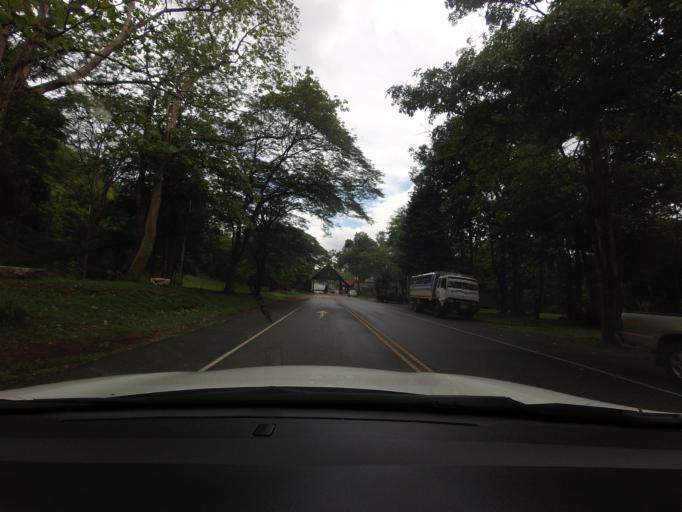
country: TH
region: Nakhon Ratchasima
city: Pak Chong
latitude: 14.5070
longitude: 101.3795
